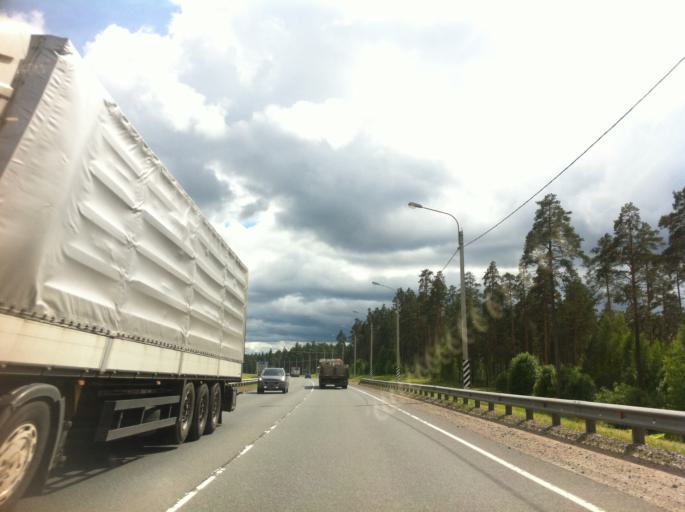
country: RU
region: Leningrad
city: Luga
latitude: 58.7237
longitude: 29.8782
